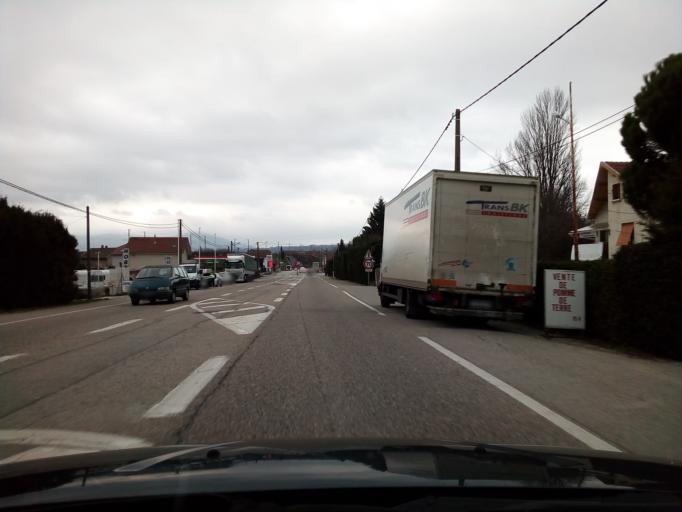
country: FR
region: Rhone-Alpes
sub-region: Departement de l'Isere
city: Saint-Jean-de-Moirans
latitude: 45.3266
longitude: 5.5784
